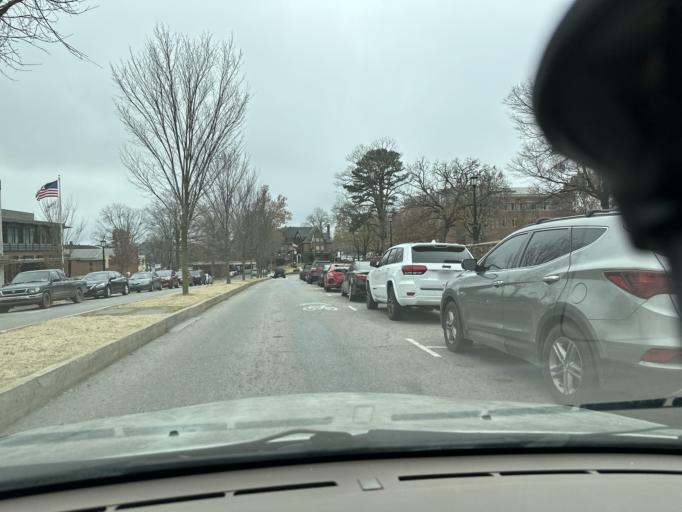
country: US
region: Arkansas
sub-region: Washington County
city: Fayetteville
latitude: 36.0676
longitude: -94.1686
